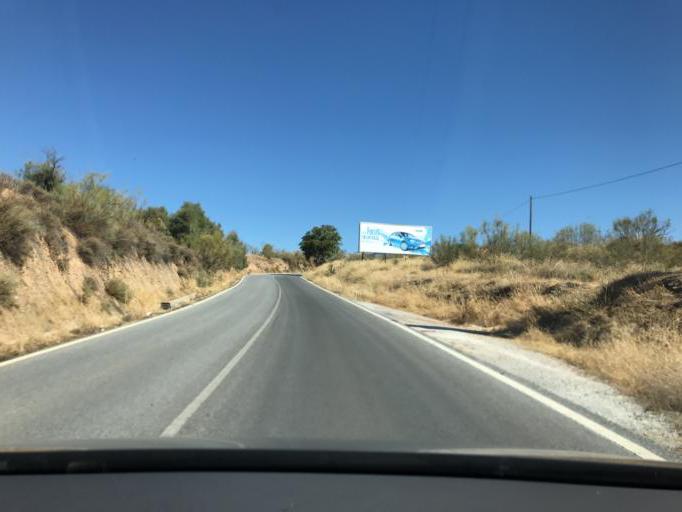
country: ES
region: Andalusia
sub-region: Provincia de Granada
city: Jun
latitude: 37.2017
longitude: -3.5895
